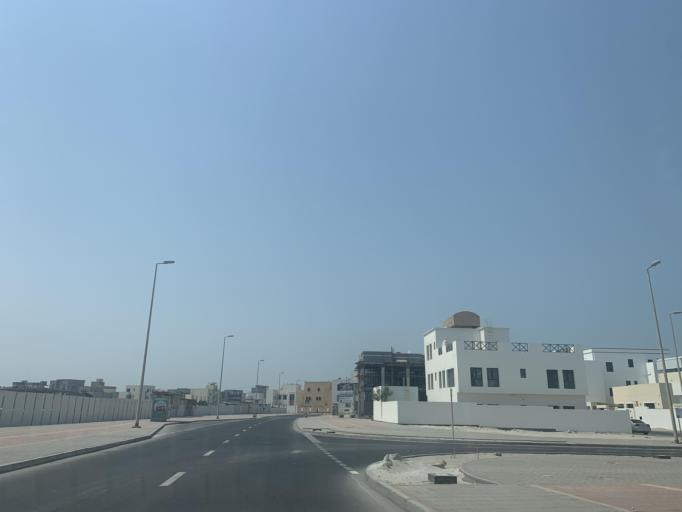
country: BH
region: Muharraq
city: Al Hadd
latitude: 26.2375
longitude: 50.6616
